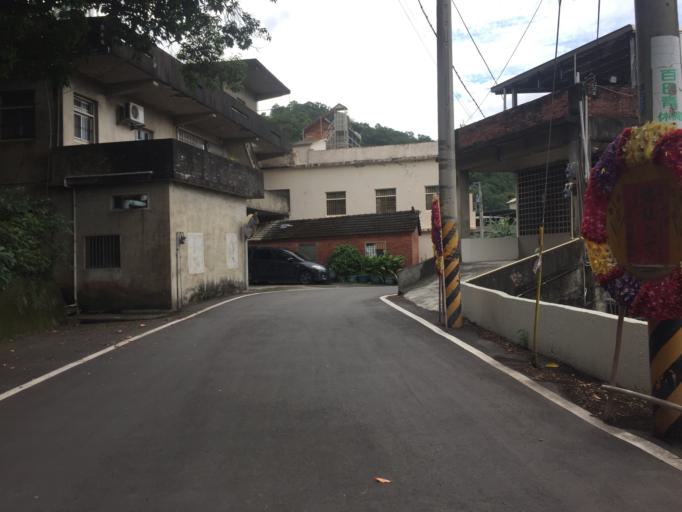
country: TW
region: Taiwan
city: Daxi
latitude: 24.7896
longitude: 121.1668
